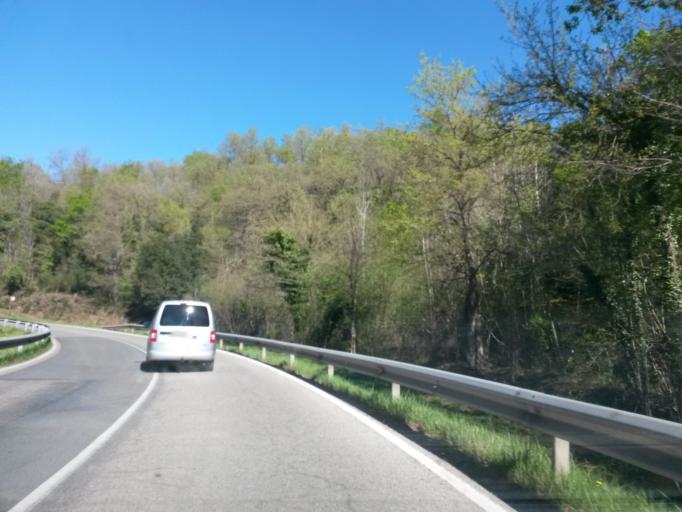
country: ES
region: Catalonia
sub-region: Provincia de Girona
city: Sant Cristofol de les Fonts
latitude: 42.1529
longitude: 2.5239
